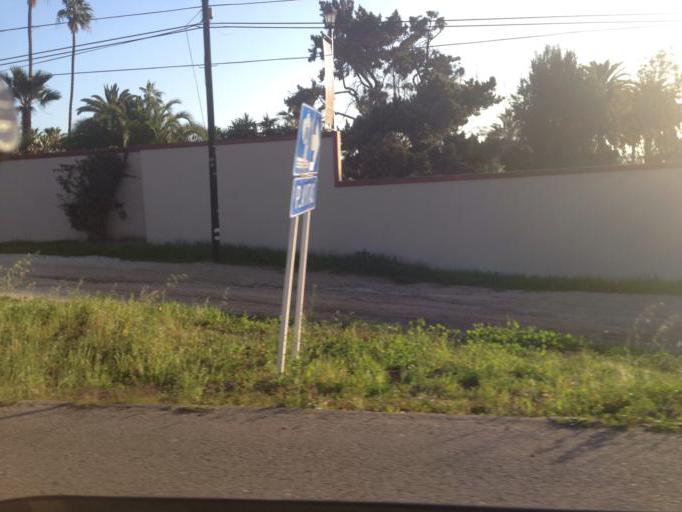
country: MX
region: Baja California
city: El Sauzal
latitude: 31.8647
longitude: -116.6578
